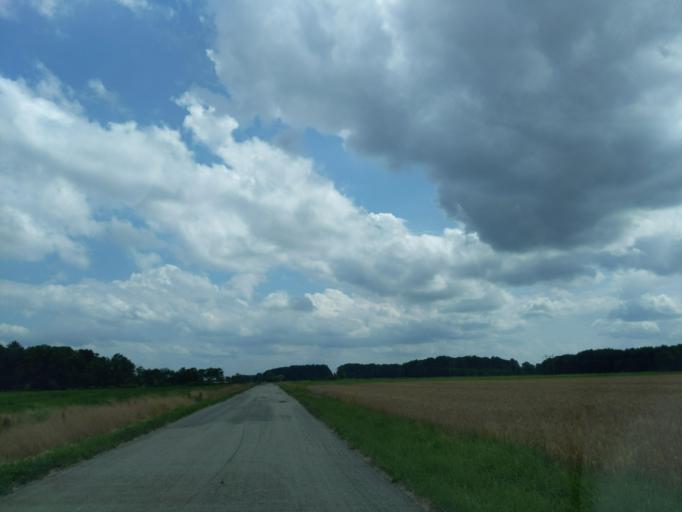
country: US
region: Indiana
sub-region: Ripley County
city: Batesville
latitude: 39.3132
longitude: -85.1896
